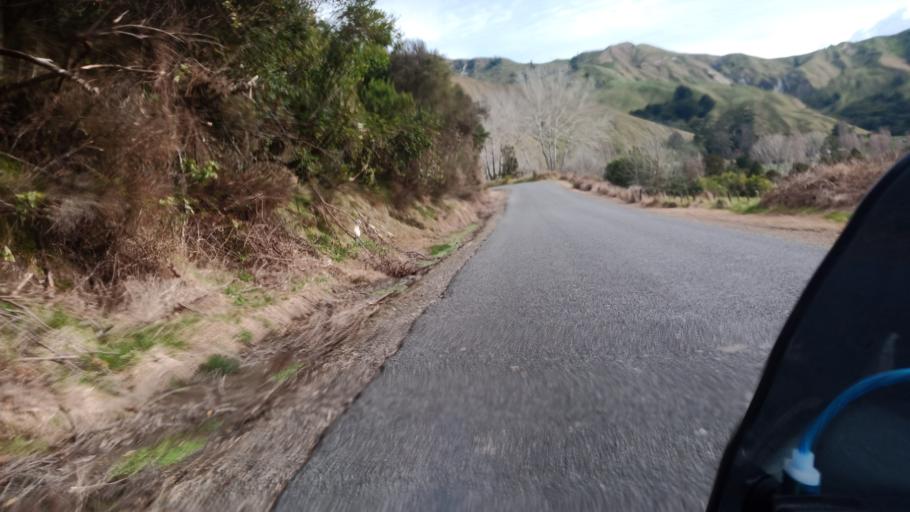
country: NZ
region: Hawke's Bay
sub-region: Wairoa District
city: Wairoa
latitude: -38.7958
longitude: 177.4430
